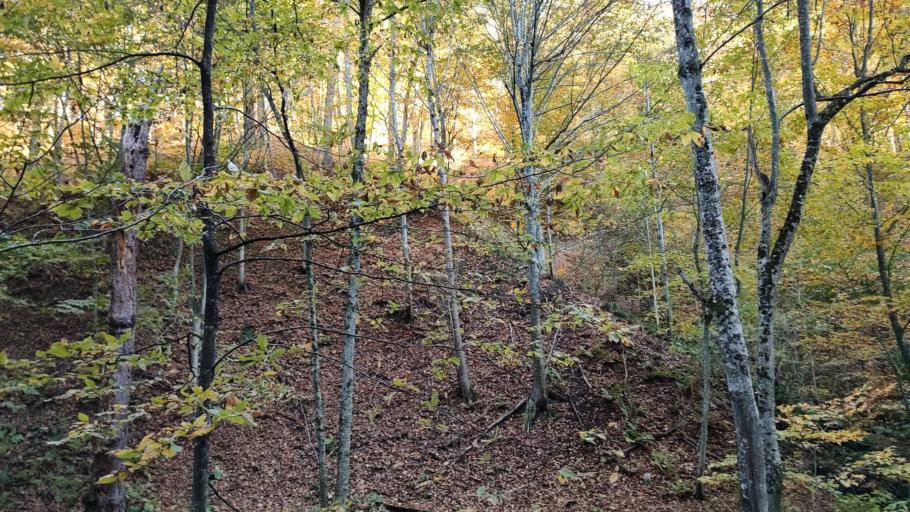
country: RU
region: Krasnodarskiy
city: Goryachiy Klyuch
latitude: 44.5955
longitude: 39.1230
